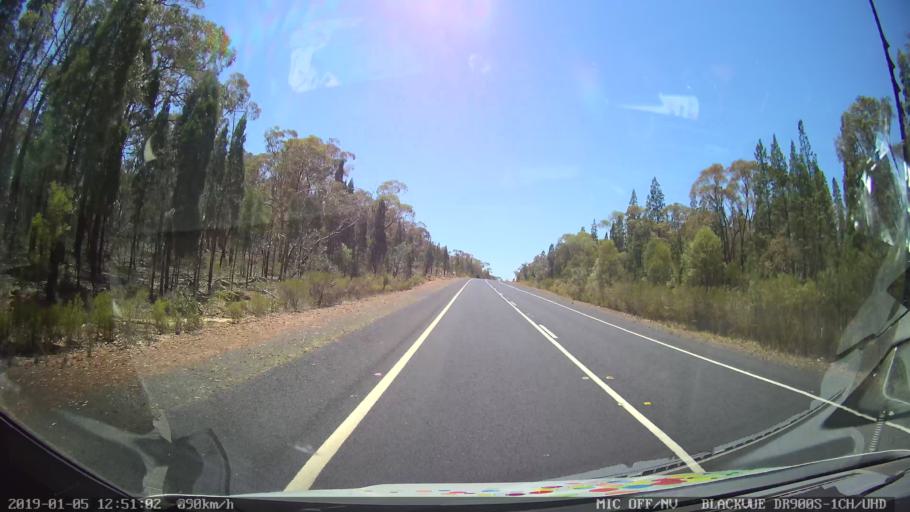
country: AU
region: New South Wales
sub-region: Warrumbungle Shire
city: Coonabarabran
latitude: -31.1204
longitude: 149.6329
